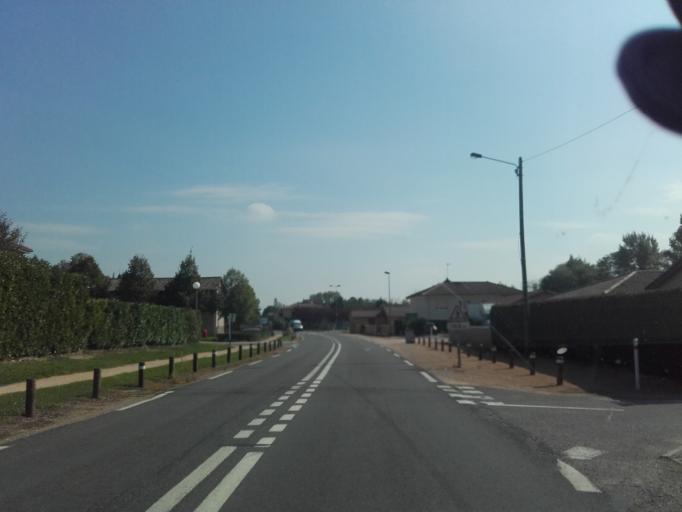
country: FR
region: Bourgogne
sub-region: Departement de Saone-et-Loire
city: La Chapelle-de-Guinchay
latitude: 46.2105
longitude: 4.7655
